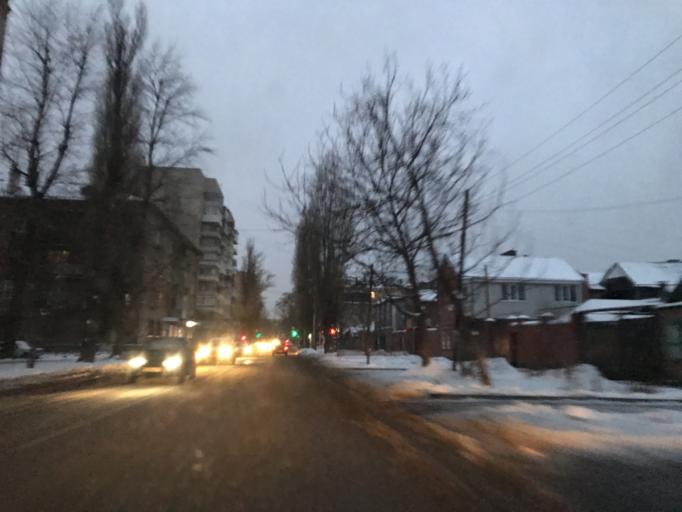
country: RU
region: Rostov
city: Imeni Chkalova
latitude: 47.2494
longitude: 39.7704
